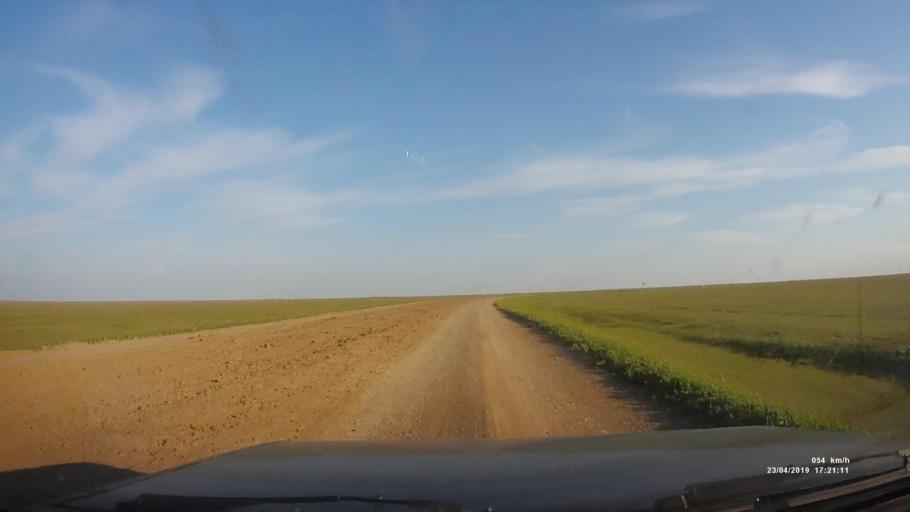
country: RU
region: Kalmykiya
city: Priyutnoye
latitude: 46.1780
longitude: 43.5043
